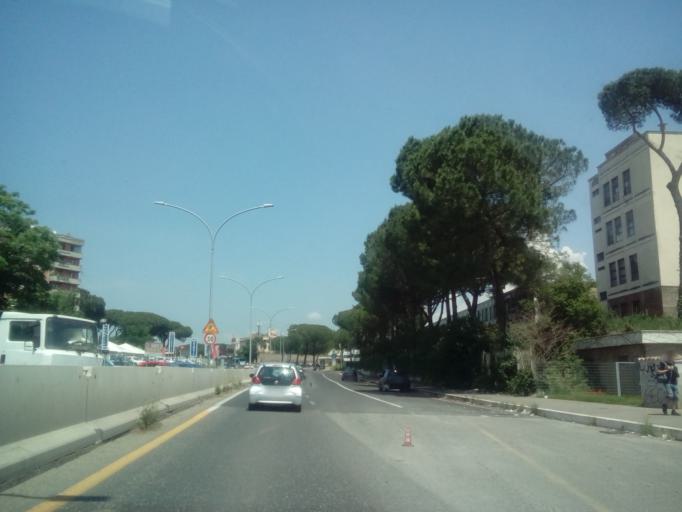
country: IT
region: Latium
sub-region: Citta metropolitana di Roma Capitale
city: Colle Verde
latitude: 41.9277
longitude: 12.5756
